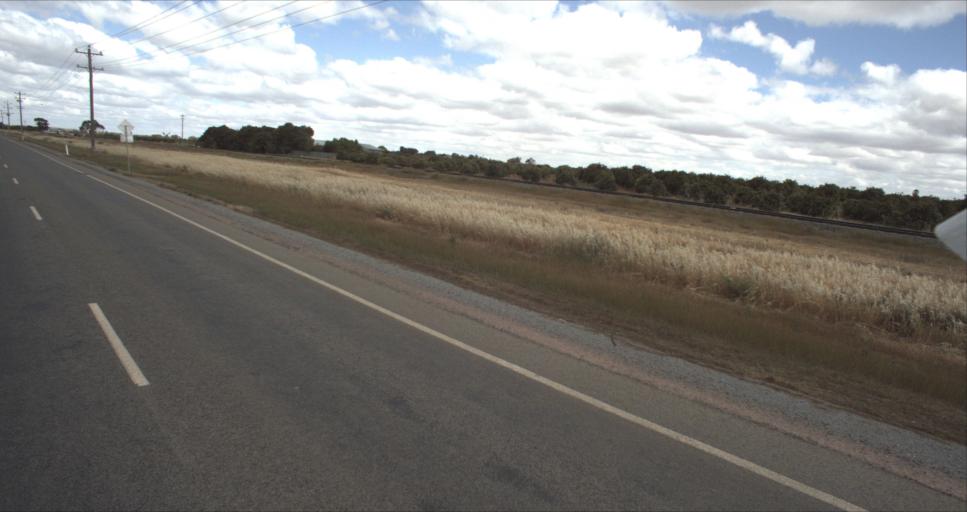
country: AU
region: New South Wales
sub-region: Leeton
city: Leeton
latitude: -34.5768
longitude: 146.3959
